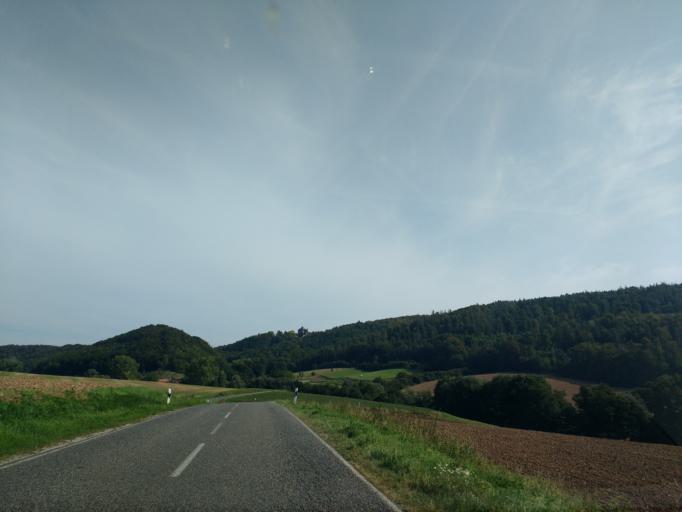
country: DE
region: Hesse
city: Witzenhausen
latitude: 51.3870
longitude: 9.8187
